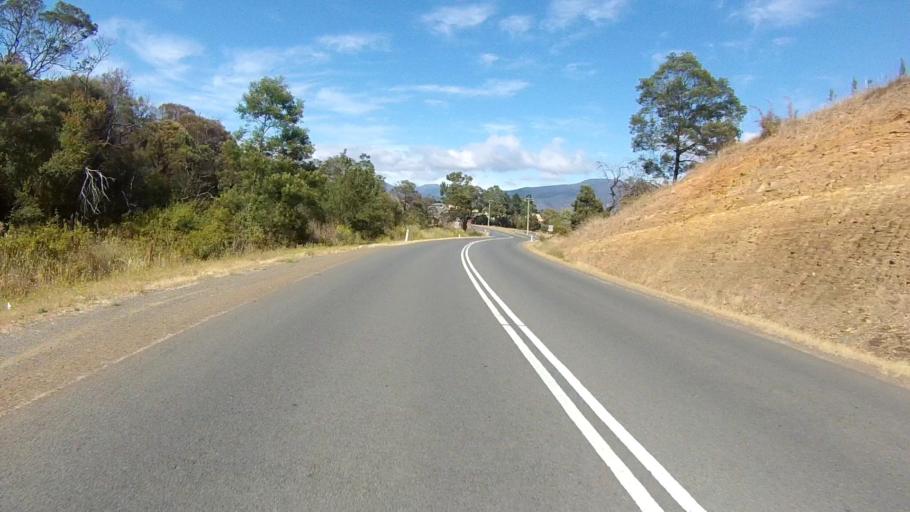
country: AU
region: Tasmania
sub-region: Brighton
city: Old Beach
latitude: -42.7444
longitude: 147.2831
